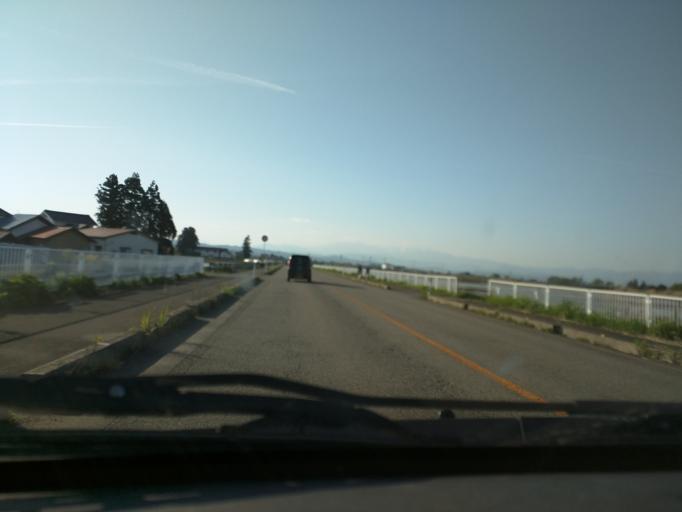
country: JP
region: Fukushima
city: Kitakata
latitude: 37.4803
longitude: 139.8511
